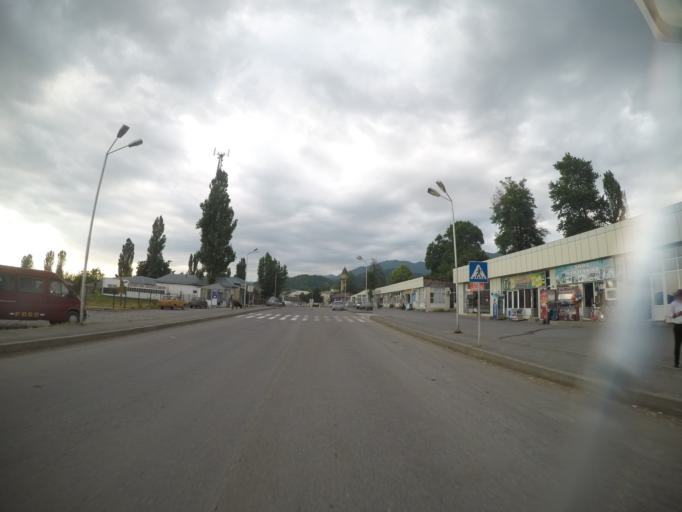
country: AZ
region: Qabala Rayon
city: Qutqashen
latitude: 40.9459
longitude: 47.9428
